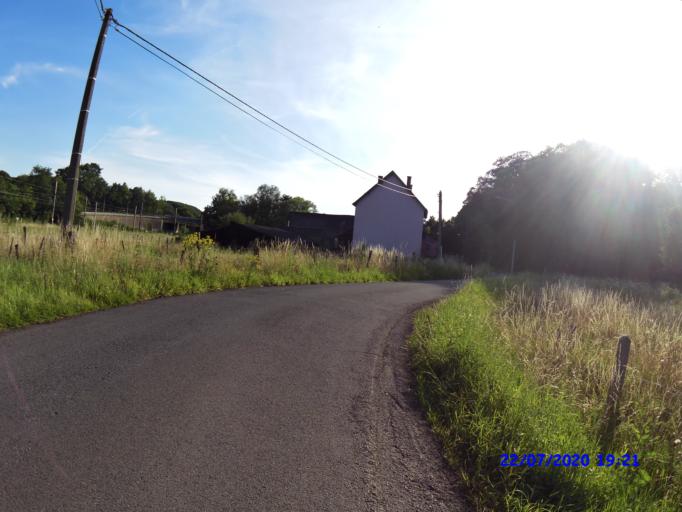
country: BE
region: Flanders
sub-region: Provincie Vlaams-Brabant
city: Aarschot
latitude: 50.9796
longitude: 4.8174
